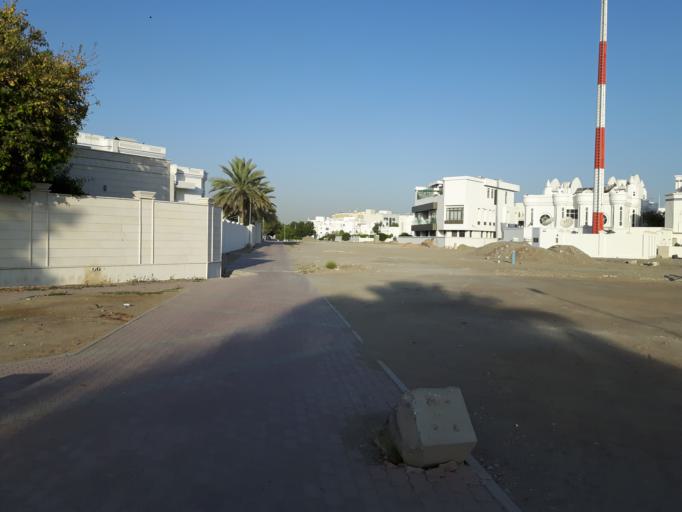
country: OM
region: Muhafazat Masqat
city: Bawshar
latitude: 23.6096
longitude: 58.4502
